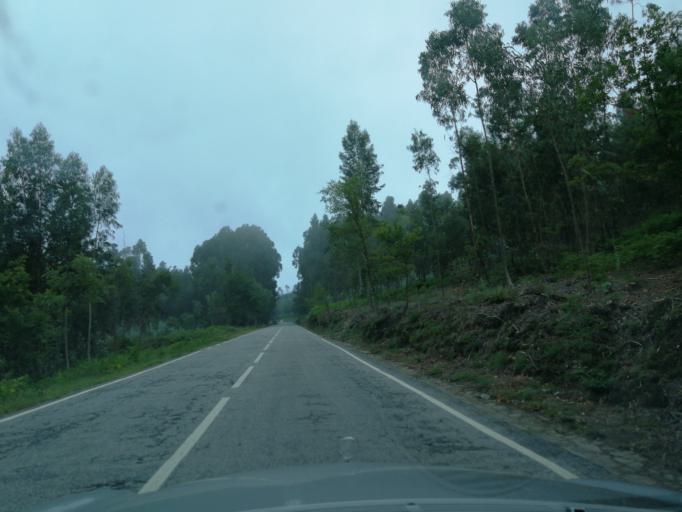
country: PT
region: Braga
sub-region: Braga
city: Braga
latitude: 41.5222
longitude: -8.3812
